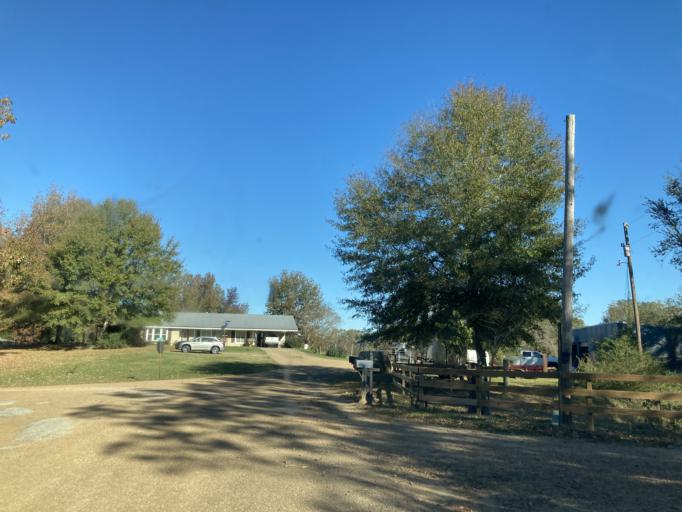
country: US
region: Mississippi
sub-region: Madison County
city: Kearney Park
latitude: 32.7131
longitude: -90.3555
